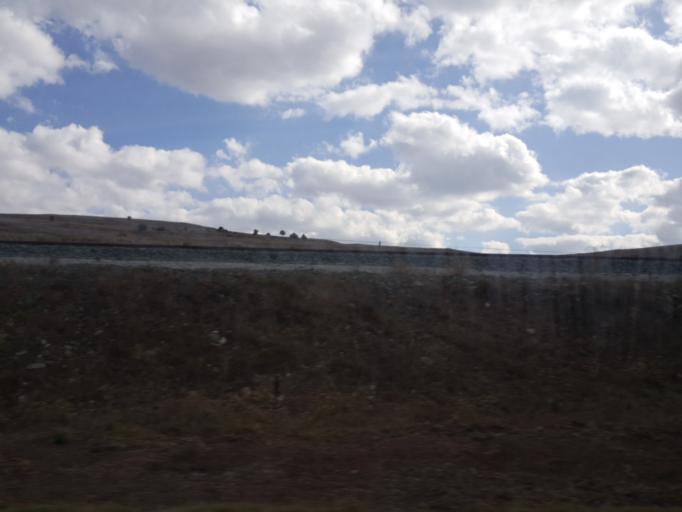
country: TR
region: Tokat
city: Yesilyurt
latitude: 40.0157
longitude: 36.2444
